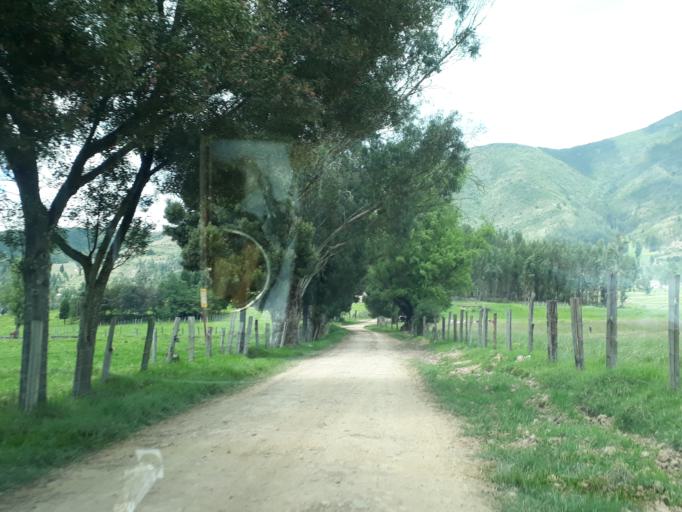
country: CO
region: Boyaca
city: Floresta
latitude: 5.8554
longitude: -72.9511
